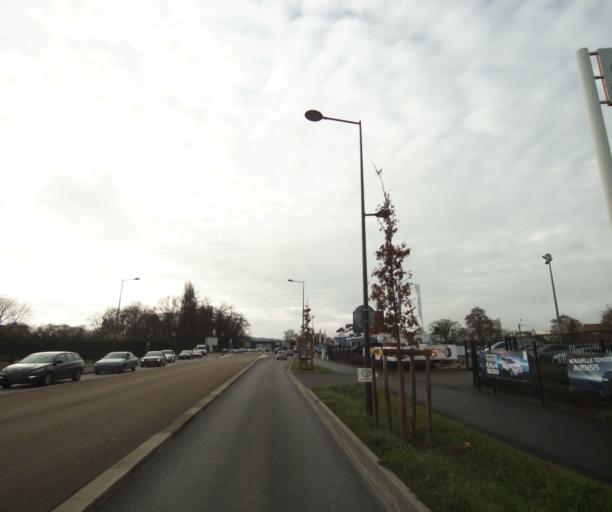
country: FR
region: Pays de la Loire
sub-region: Departement de la Sarthe
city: Allonnes
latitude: 47.9837
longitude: 0.1772
